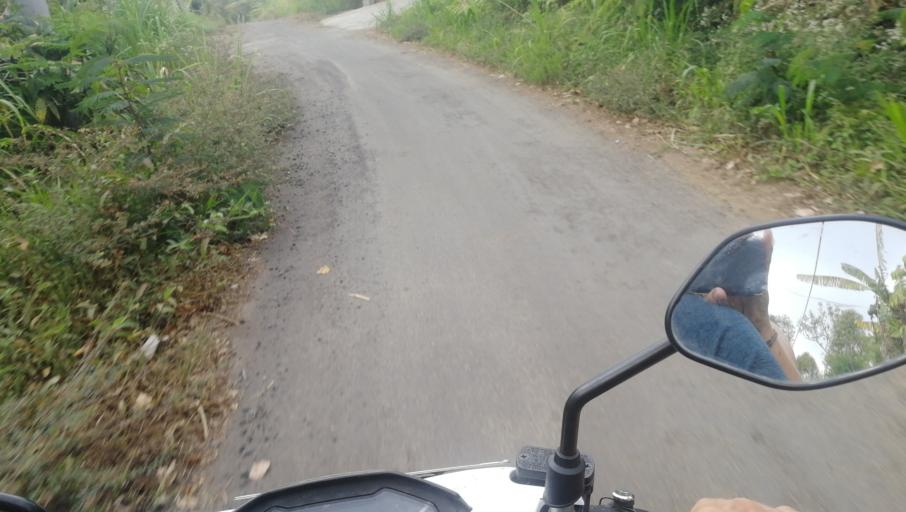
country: ID
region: Bali
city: Banjar Ambengan
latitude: -8.2102
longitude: 115.1107
